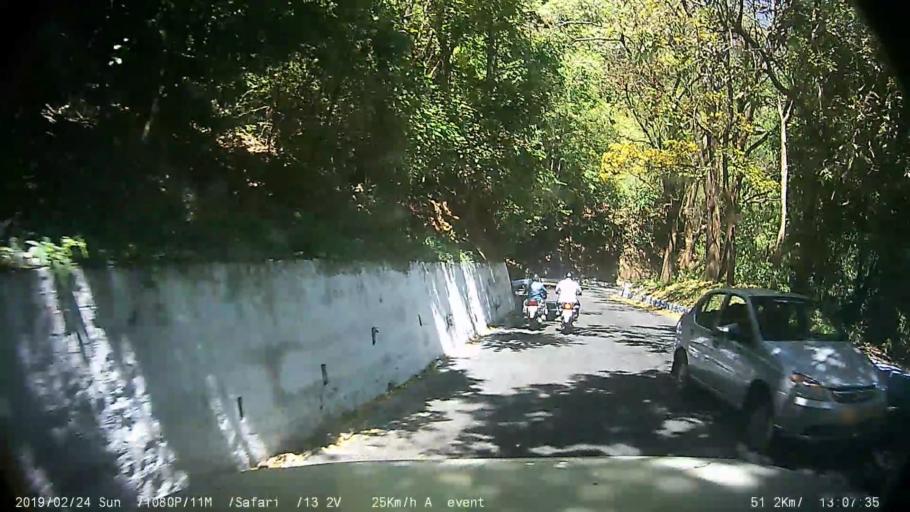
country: IN
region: Tamil Nadu
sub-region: Nilgiri
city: Wellington
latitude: 11.3384
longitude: 76.8347
